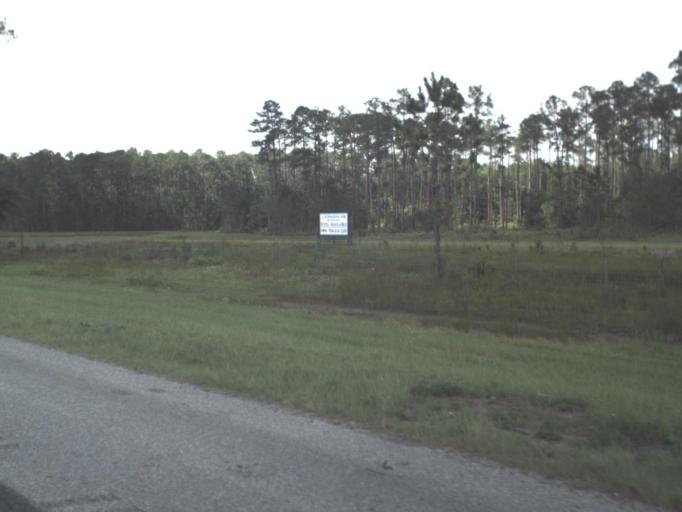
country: US
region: Florida
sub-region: Saint Johns County
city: Villano Beach
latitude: 29.9945
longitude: -81.4667
